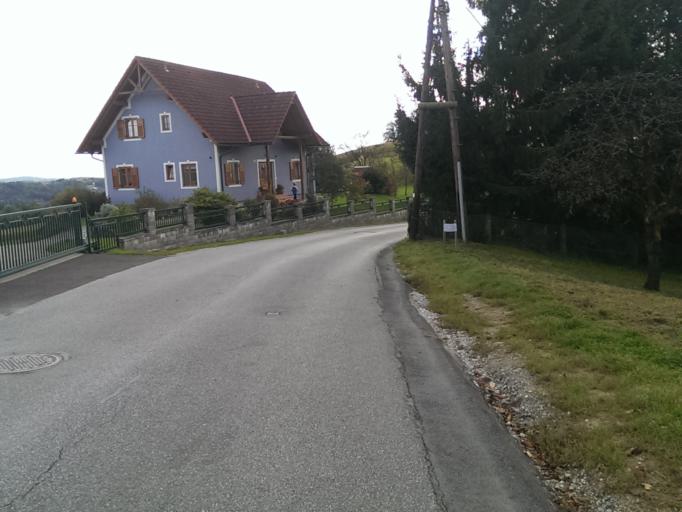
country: AT
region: Styria
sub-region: Politischer Bezirk Graz-Umgebung
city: Hart bei Graz
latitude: 47.0618
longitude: 15.5042
